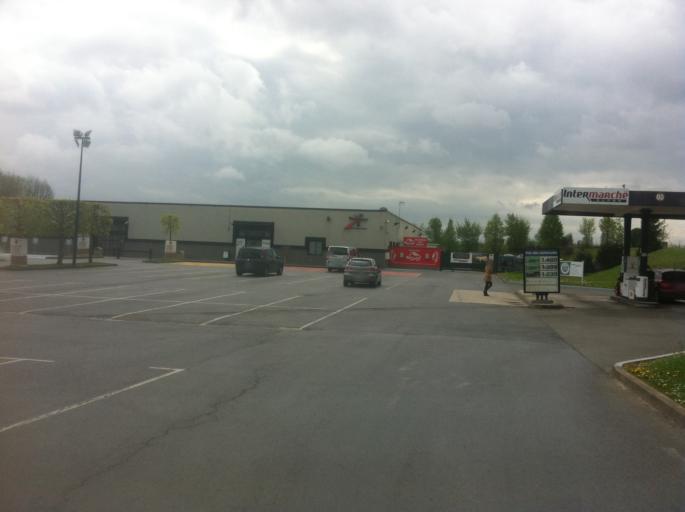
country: FR
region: Picardie
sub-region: Departement de l'Oise
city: Nanteuil-le-Haudouin
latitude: 49.1366
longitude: 2.8033
